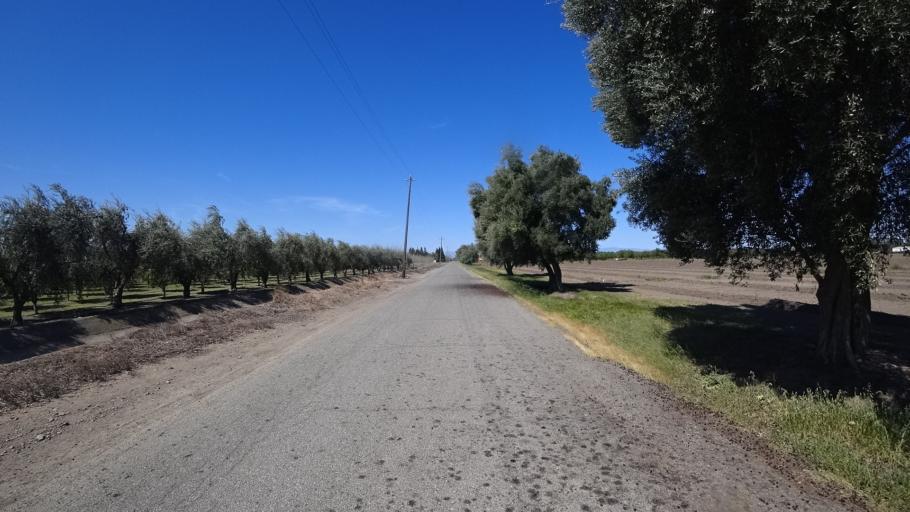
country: US
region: California
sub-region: Glenn County
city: Orland
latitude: 39.7431
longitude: -122.1145
